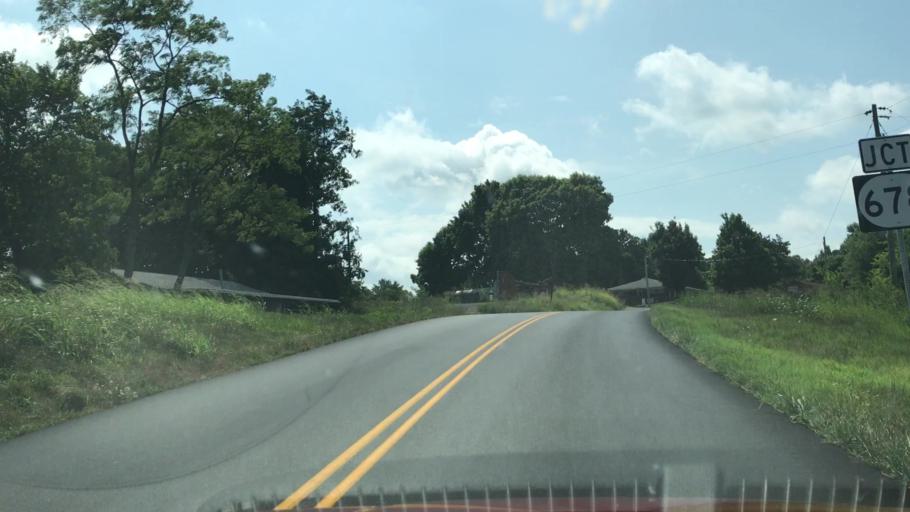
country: US
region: Kentucky
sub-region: Monroe County
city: Tompkinsville
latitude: 36.8080
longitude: -85.8215
